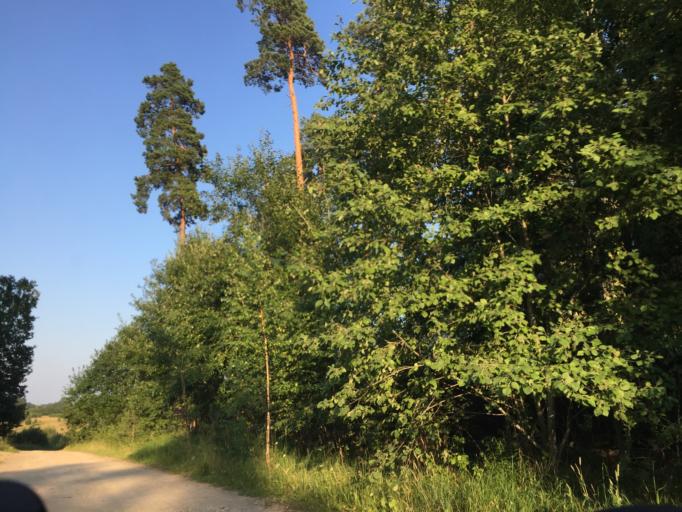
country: LV
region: Garkalne
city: Garkalne
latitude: 56.9785
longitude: 24.3794
